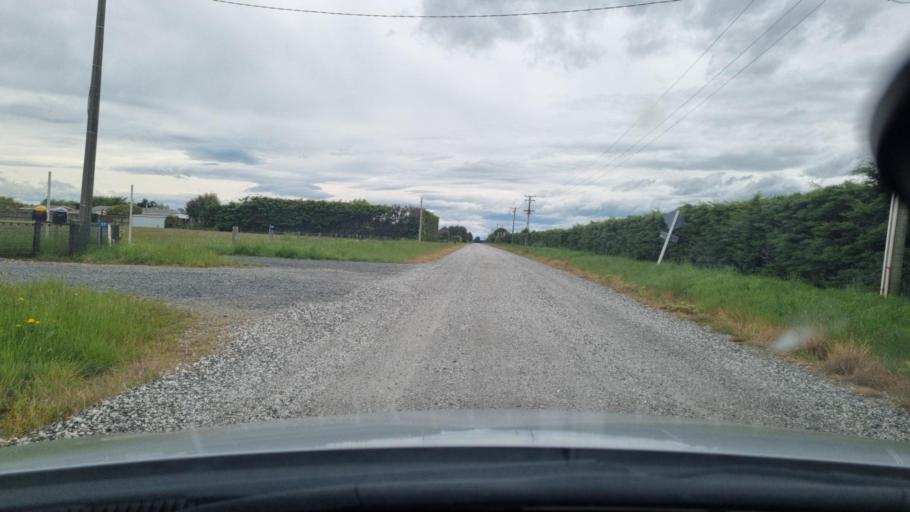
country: NZ
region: Southland
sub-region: Invercargill City
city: Invercargill
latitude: -46.3769
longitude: 168.2985
